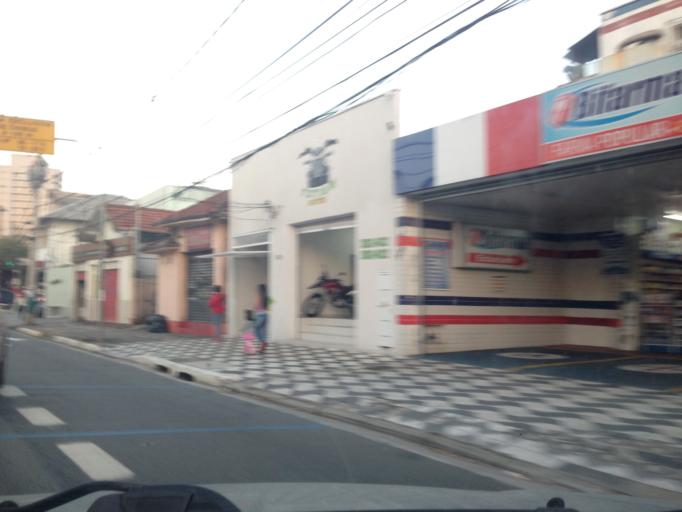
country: BR
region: Sao Paulo
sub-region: Sao Paulo
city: Sao Paulo
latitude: -23.5245
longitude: -46.7072
